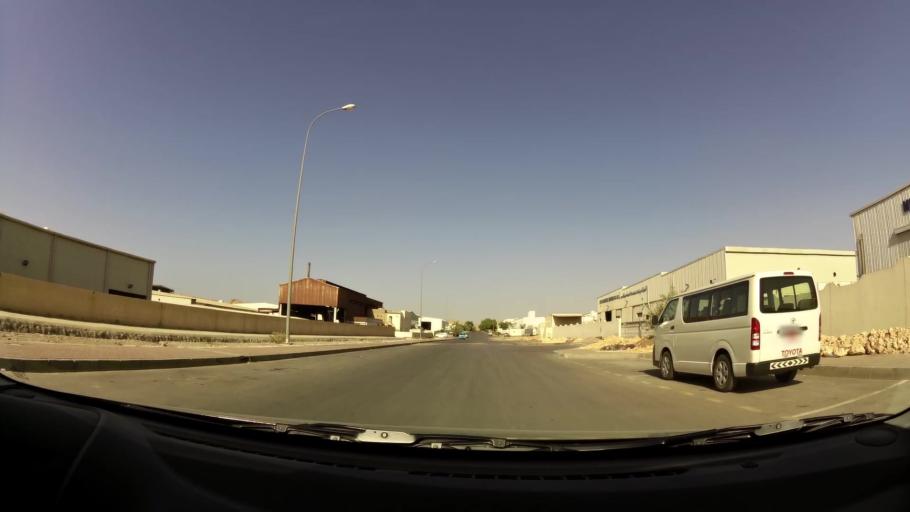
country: OM
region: Muhafazat Masqat
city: As Sib al Jadidah
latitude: 23.5520
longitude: 58.2180
